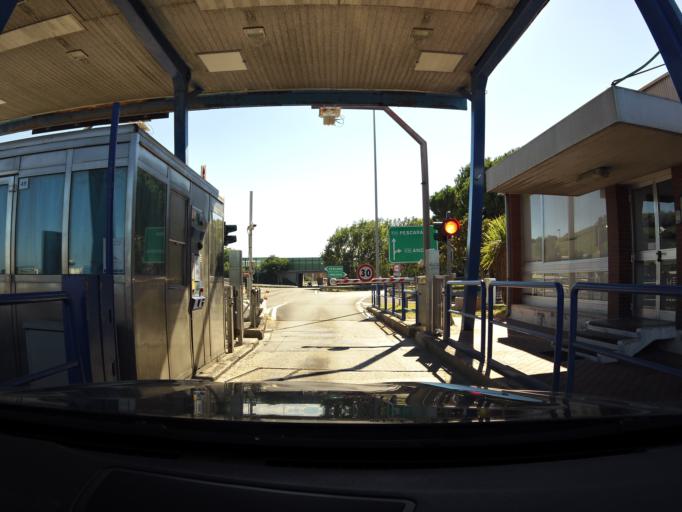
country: IT
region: The Marches
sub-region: Province of Fermo
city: Porto San Giorgio
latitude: 43.1613
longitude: 13.8000
